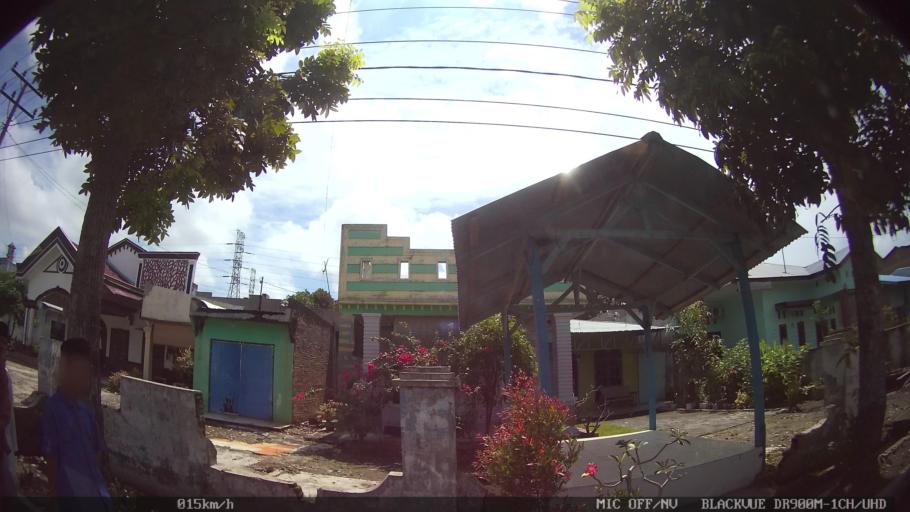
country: ID
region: North Sumatra
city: Percut
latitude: 3.6037
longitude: 98.7876
